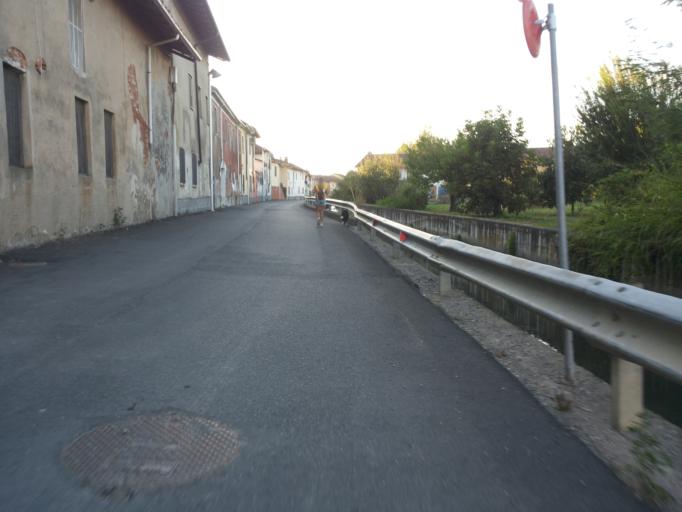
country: IT
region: Piedmont
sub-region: Provincia di Vercelli
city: Pezzana
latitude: 45.2611
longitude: 8.4918
